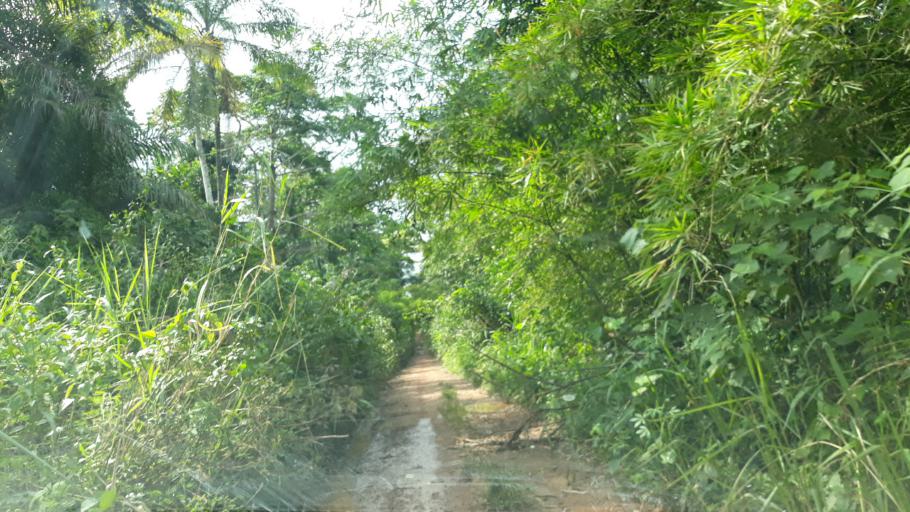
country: CD
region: Maniema
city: Kampene
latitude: -2.7715
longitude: 26.9319
